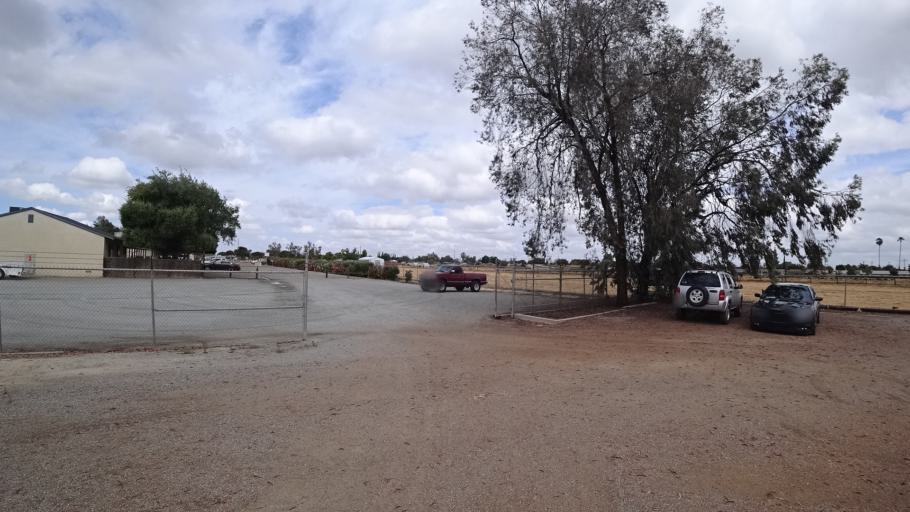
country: US
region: California
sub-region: Kings County
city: Home Garden
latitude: 36.3018
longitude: -119.6514
